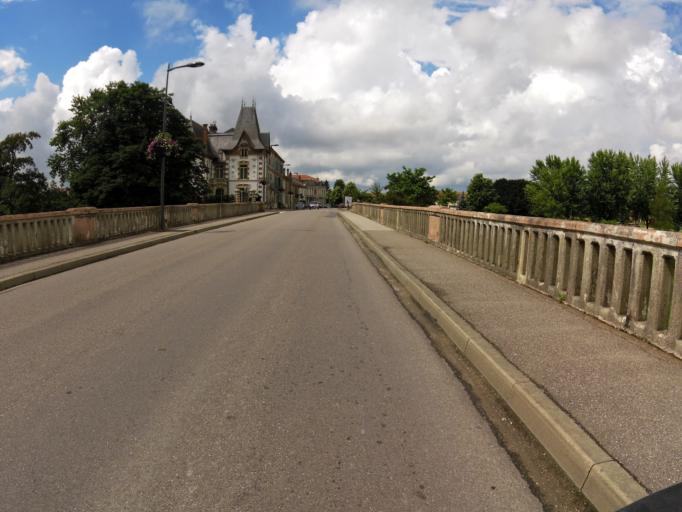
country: FR
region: Lorraine
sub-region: Departement de la Meuse
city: Revigny-sur-Ornain
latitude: 48.8253
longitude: 4.9855
